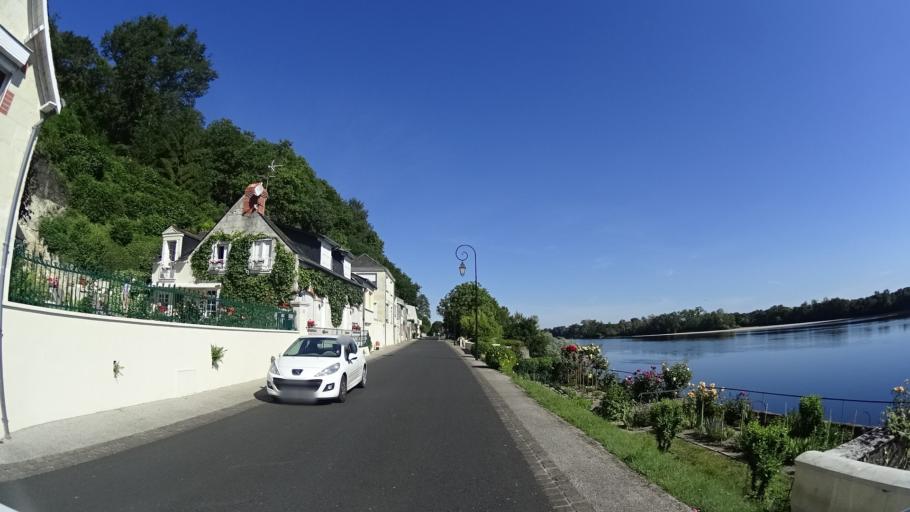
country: FR
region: Pays de la Loire
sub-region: Departement de Maine-et-Loire
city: Saint-Martin-de-la-Place
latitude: 47.3001
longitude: -0.1423
